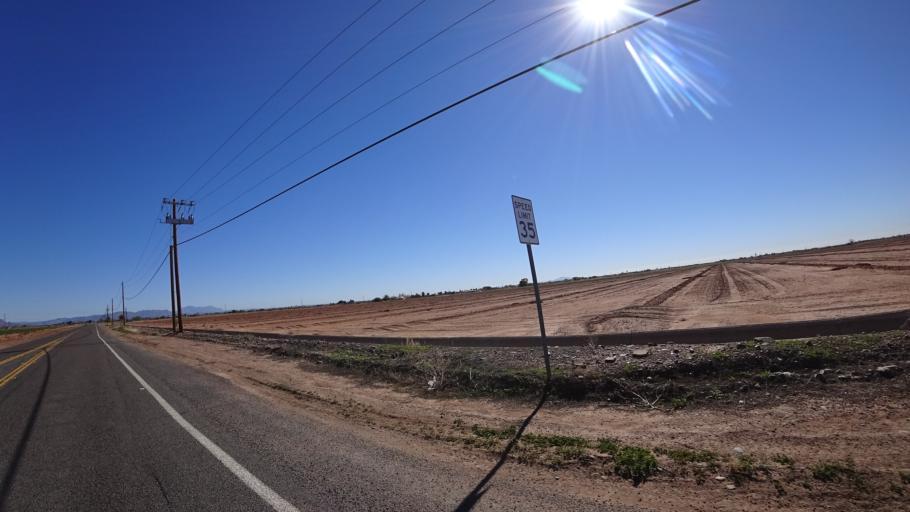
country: US
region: Arizona
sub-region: Maricopa County
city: Scottsdale
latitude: 33.5095
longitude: -111.8782
